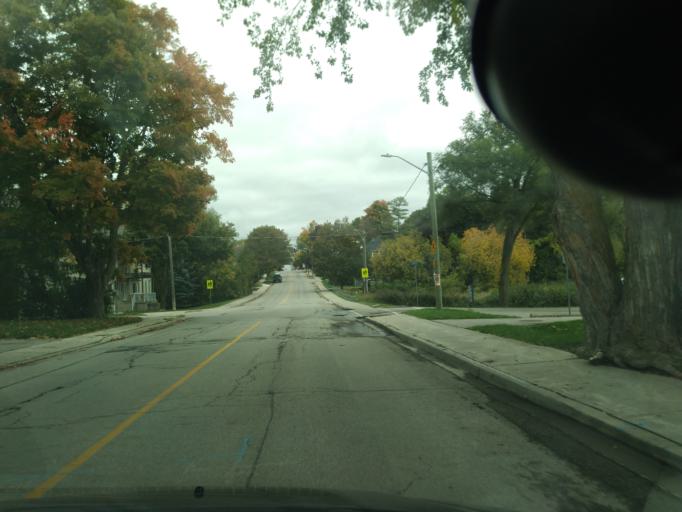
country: CA
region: Ontario
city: Newmarket
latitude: 44.0498
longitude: -79.4631
